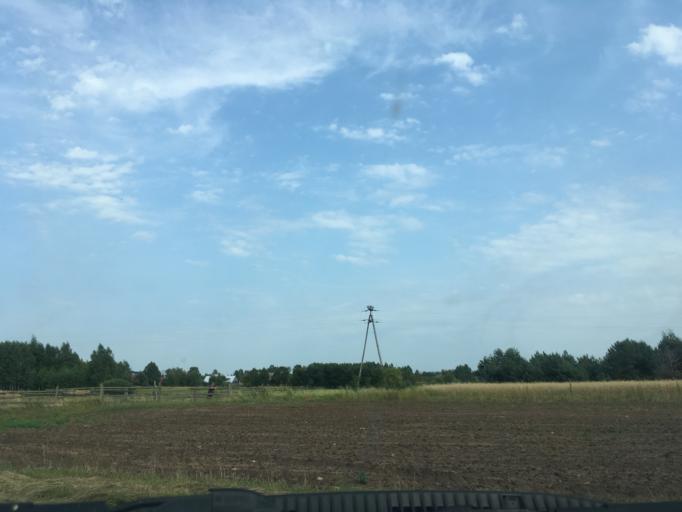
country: PL
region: Podlasie
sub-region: Powiat hajnowski
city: Bialowieza
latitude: 52.8952
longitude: 23.8332
